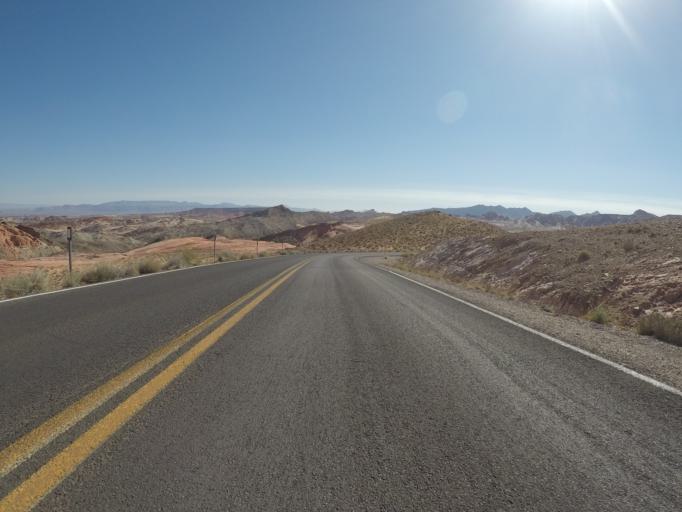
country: US
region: Nevada
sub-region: Clark County
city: Moapa Valley
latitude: 36.4872
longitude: -114.5269
